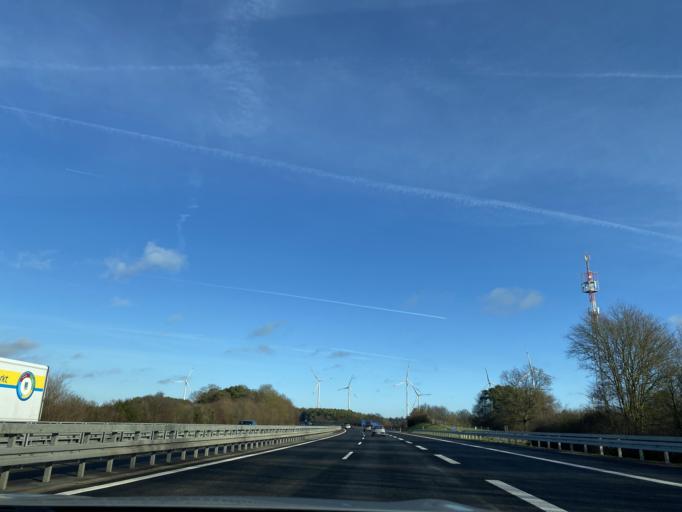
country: DE
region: Baden-Wuerttemberg
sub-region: Regierungsbezirk Stuttgart
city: Buch am Ahorn
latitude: 49.4660
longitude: 9.5541
